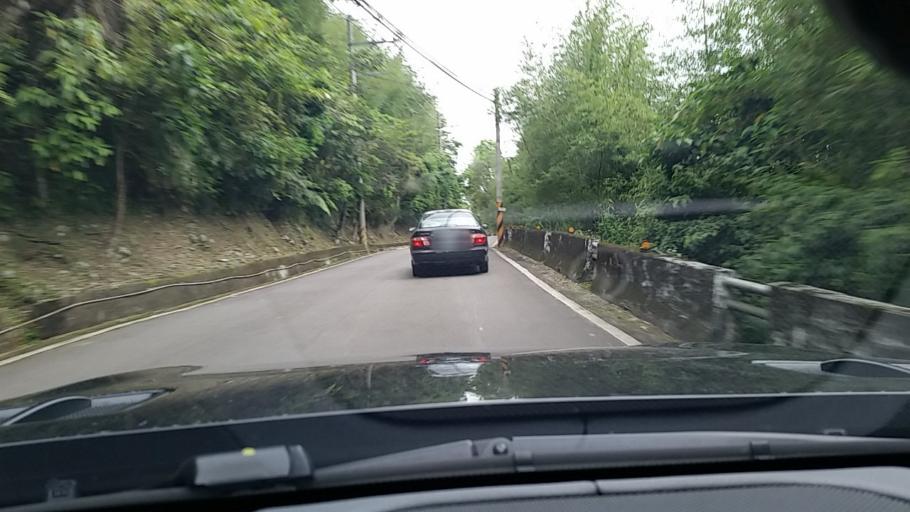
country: TW
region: Taiwan
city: Daxi
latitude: 24.7997
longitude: 121.3049
